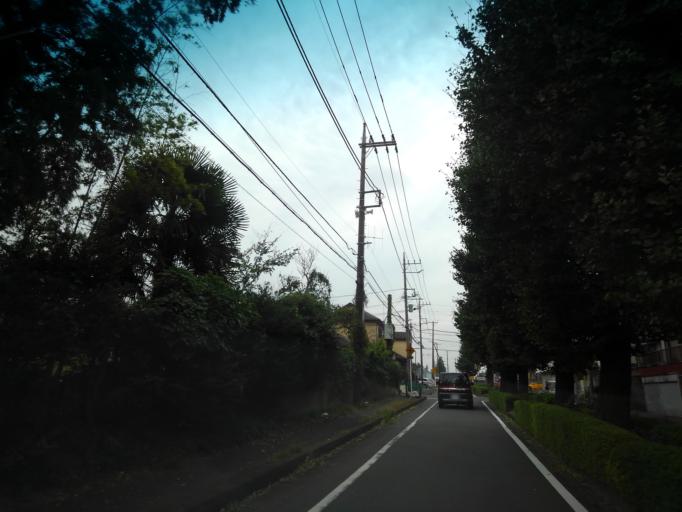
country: JP
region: Tokyo
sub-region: Machida-shi
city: Machida
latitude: 35.5869
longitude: 139.3866
